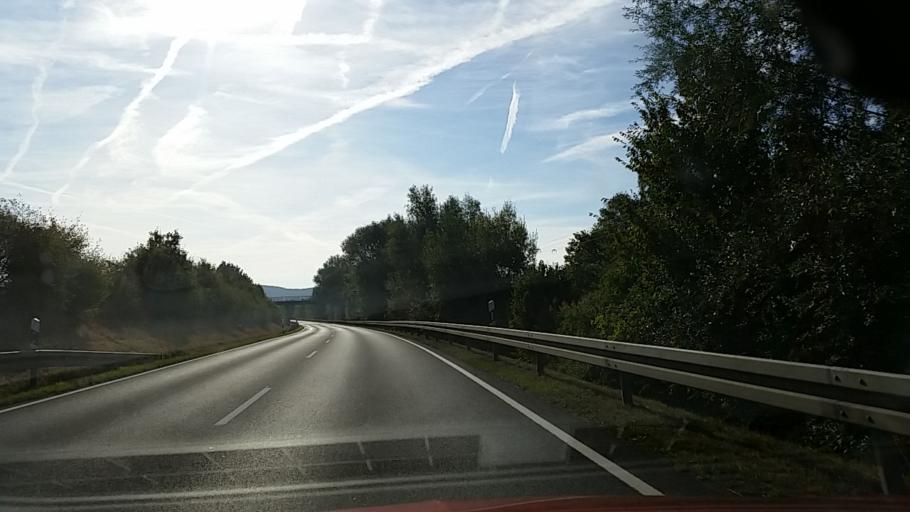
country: DE
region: Bavaria
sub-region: Regierungsbezirk Unterfranken
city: Zellingen
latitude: 49.8923
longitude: 9.8135
